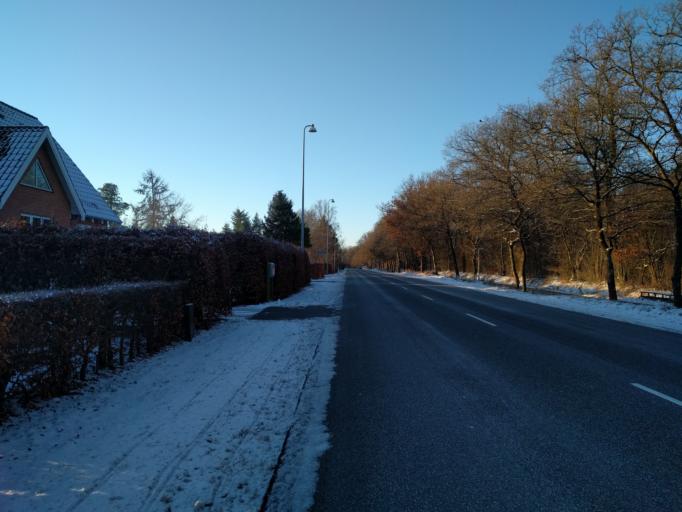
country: DK
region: Central Jutland
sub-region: Viborg Kommune
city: Viborg
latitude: 56.4274
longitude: 9.3850
